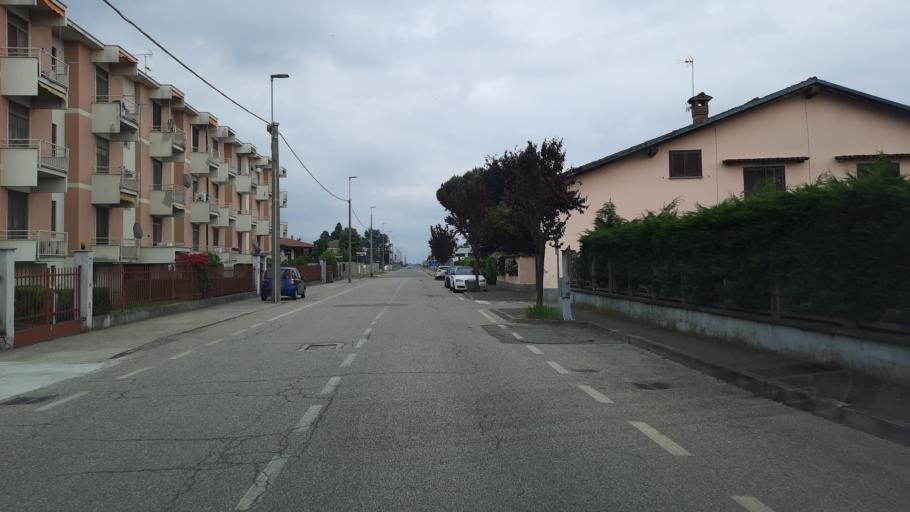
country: IT
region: Lombardy
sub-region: Provincia di Pavia
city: Robbio
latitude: 45.2843
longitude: 8.5989
